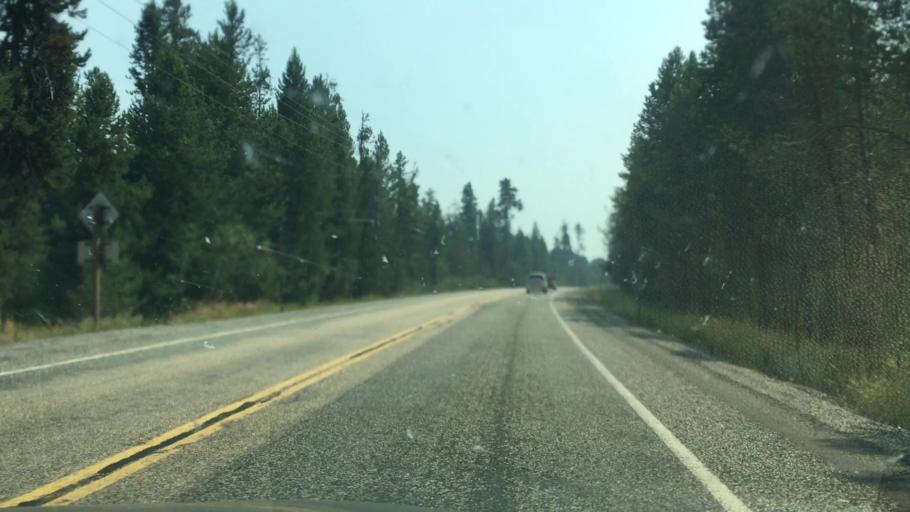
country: US
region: Idaho
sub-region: Valley County
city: Cascade
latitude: 44.4042
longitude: -116.0003
